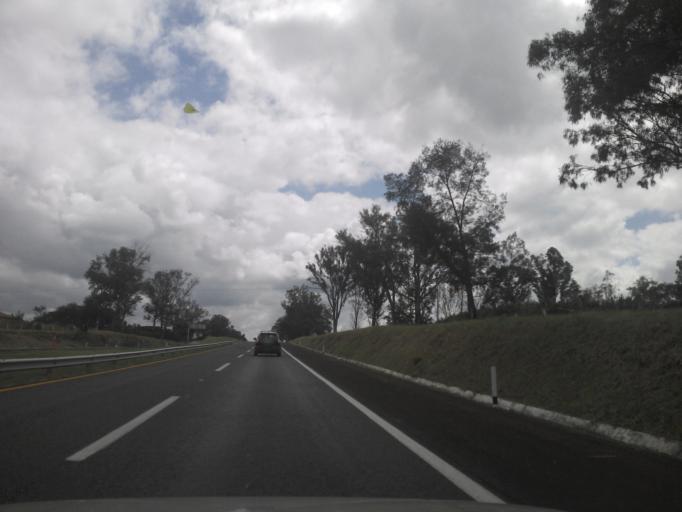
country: MX
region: Jalisco
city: Zapotlanejo
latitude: 20.6148
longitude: -103.0975
